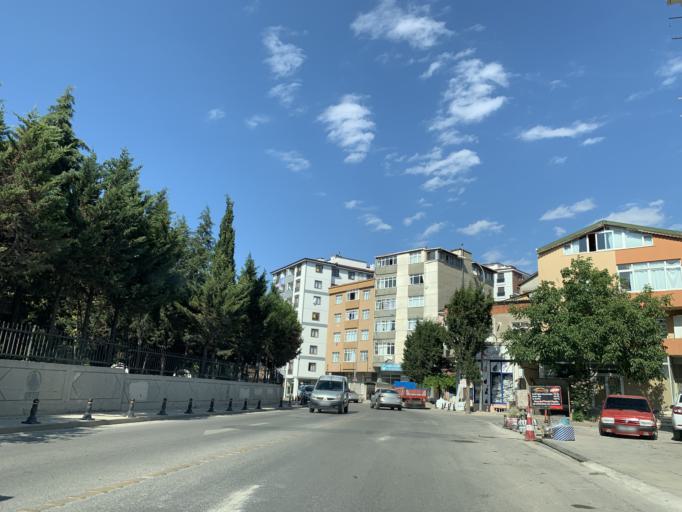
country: TR
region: Istanbul
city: Pendik
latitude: 40.8859
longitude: 29.2835
